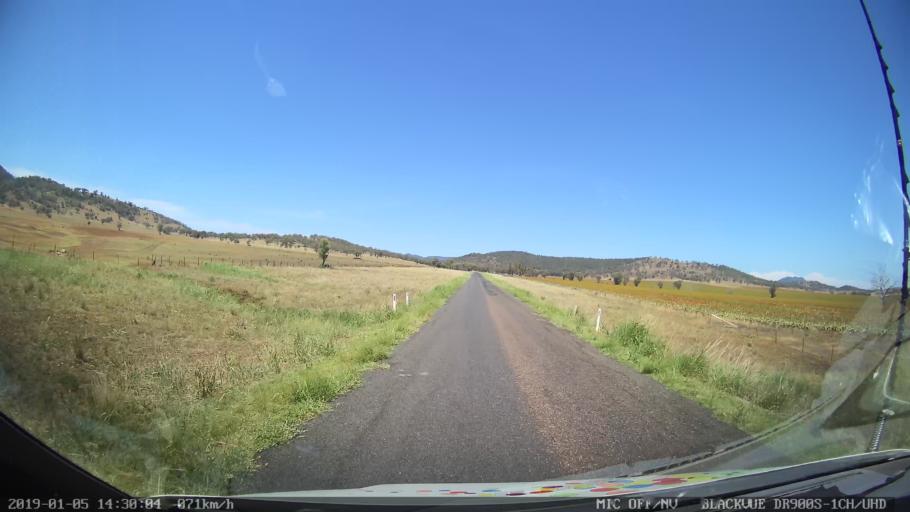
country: AU
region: New South Wales
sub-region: Tamworth Municipality
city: Phillip
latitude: -31.2281
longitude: 150.5879
